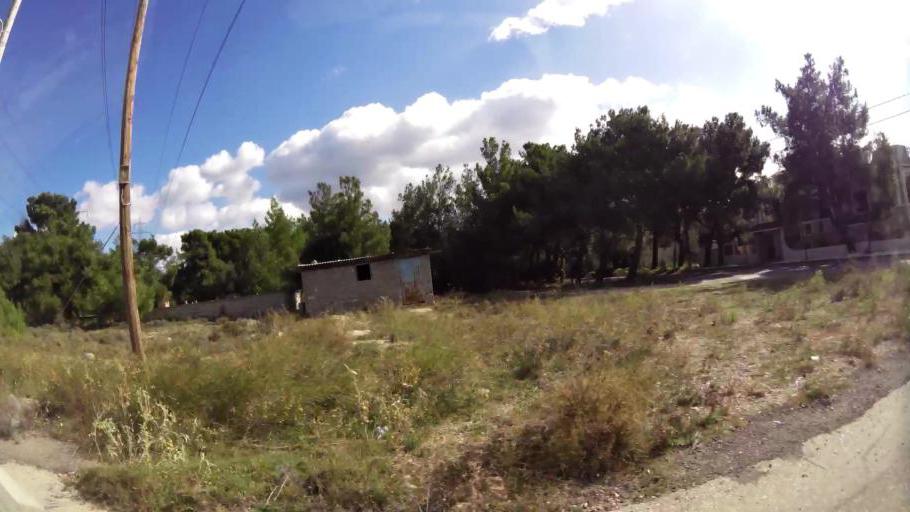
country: GR
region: Attica
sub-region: Nomarchia Anatolikis Attikis
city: Thrakomakedones
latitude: 38.1132
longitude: 23.7596
